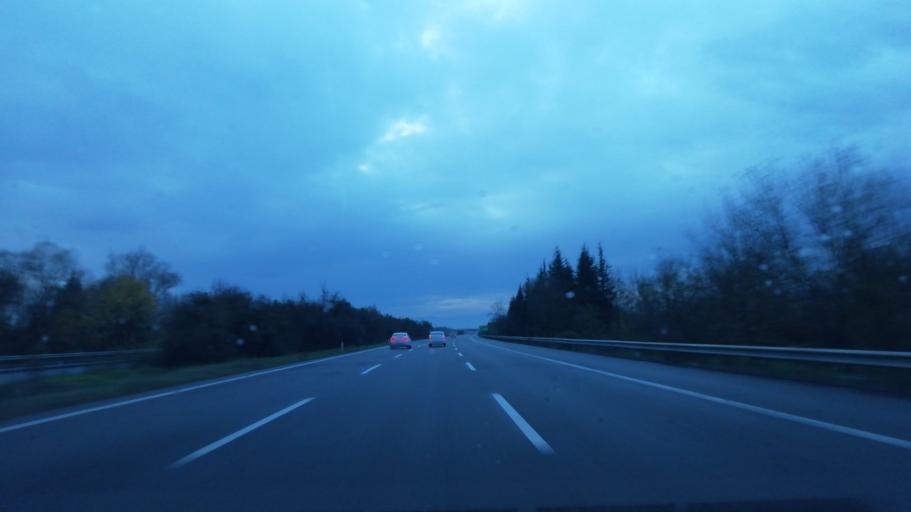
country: TR
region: Duzce
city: Duzce
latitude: 40.7944
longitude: 31.2000
